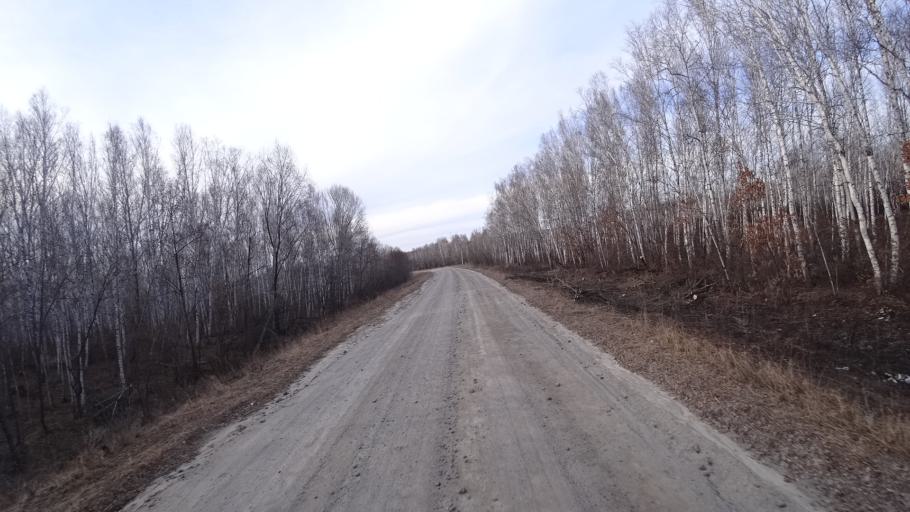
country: RU
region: Amur
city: Bureya
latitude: 50.0137
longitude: 129.7744
